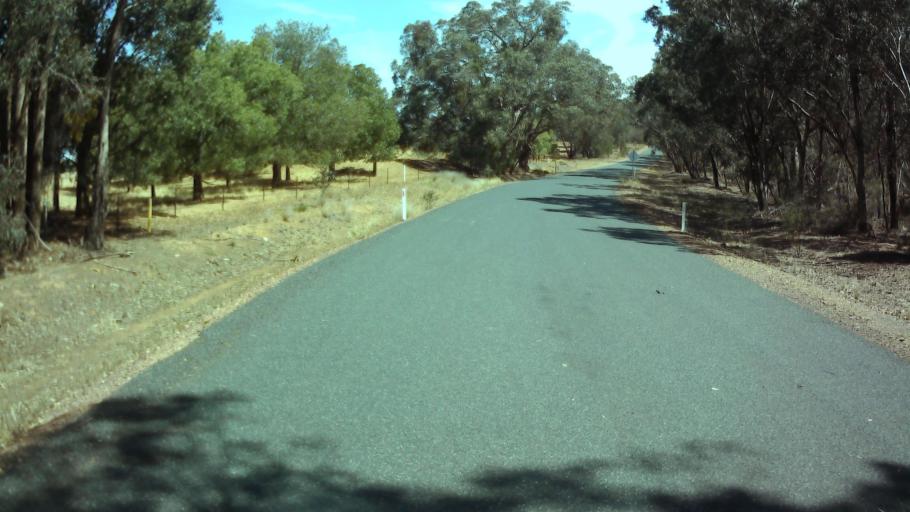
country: AU
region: New South Wales
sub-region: Weddin
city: Grenfell
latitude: -34.0019
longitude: 148.1308
